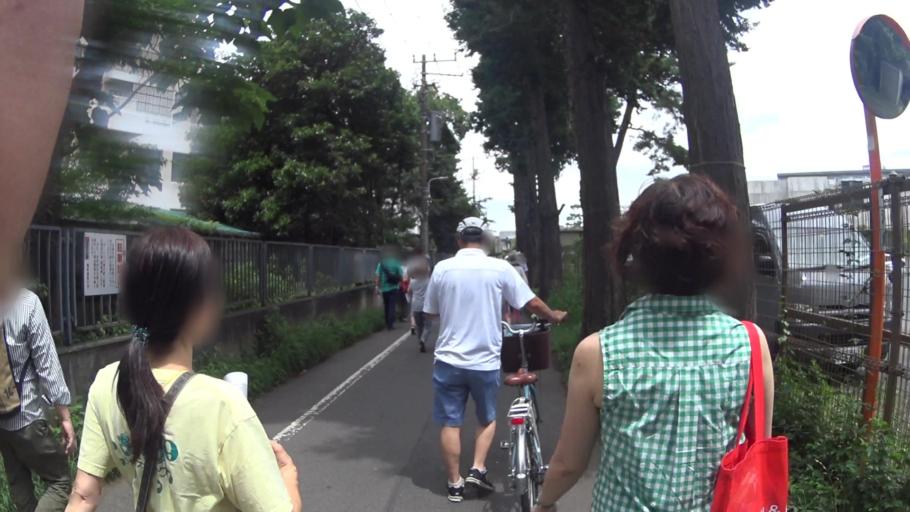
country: JP
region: Tokyo
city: Chofugaoka
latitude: 35.6572
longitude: 139.5451
